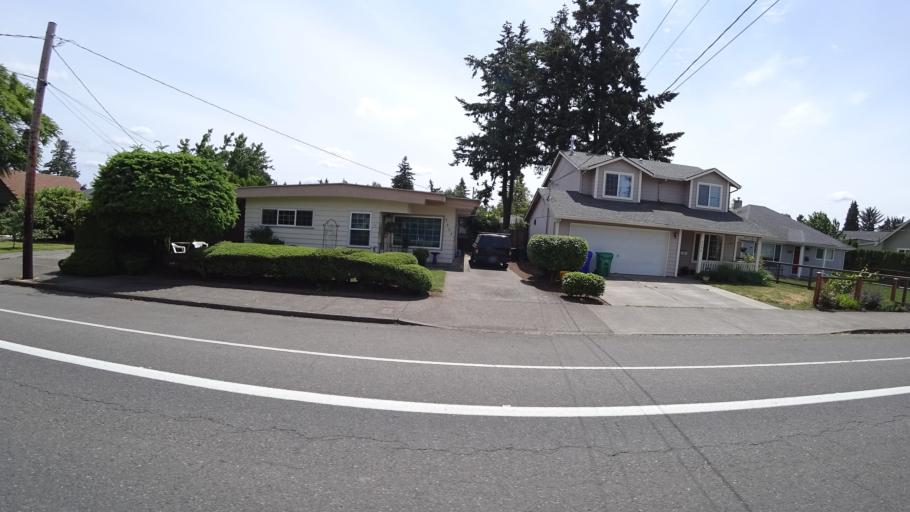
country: US
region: Oregon
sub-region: Multnomah County
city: Lents
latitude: 45.4686
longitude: -122.6056
